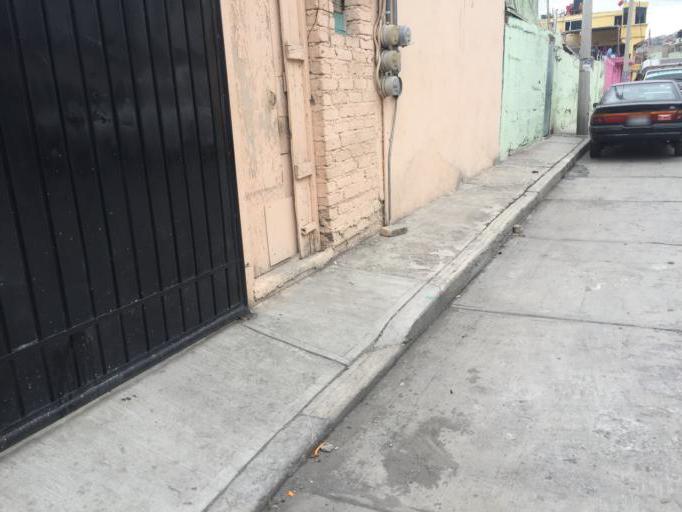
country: MX
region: Mexico
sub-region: Tlalnepantla de Baz
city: Puerto Escondido (Tepeolulco Puerto Escondido)
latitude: 19.5594
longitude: -99.0830
